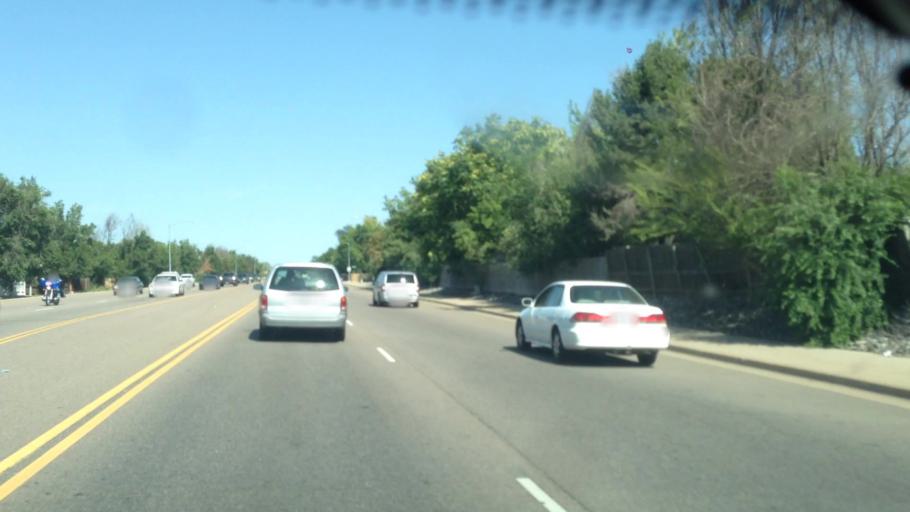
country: US
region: Colorado
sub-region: Adams County
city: Aurora
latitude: 39.7256
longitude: -104.8643
